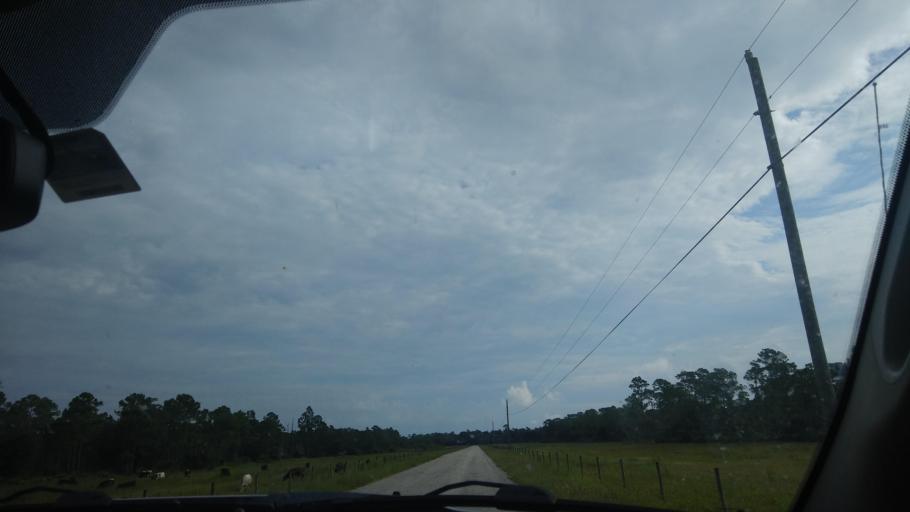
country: US
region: Florida
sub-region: Indian River County
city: Fellsmere
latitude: 27.6740
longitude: -80.8009
